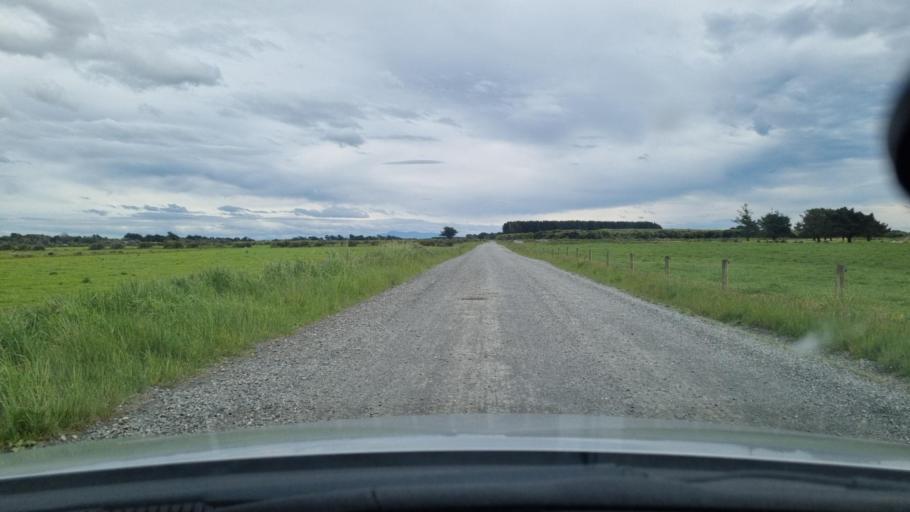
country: NZ
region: Southland
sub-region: Invercargill City
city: Invercargill
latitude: -46.4018
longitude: 168.2829
